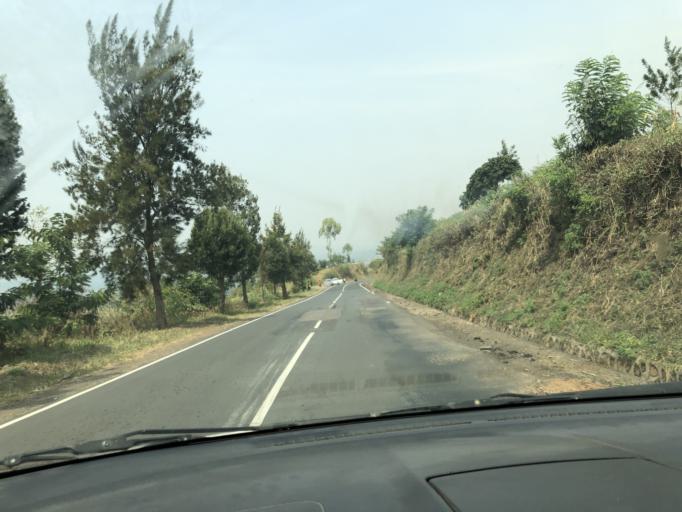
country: RW
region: Western Province
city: Cyangugu
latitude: -2.6709
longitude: 29.0037
